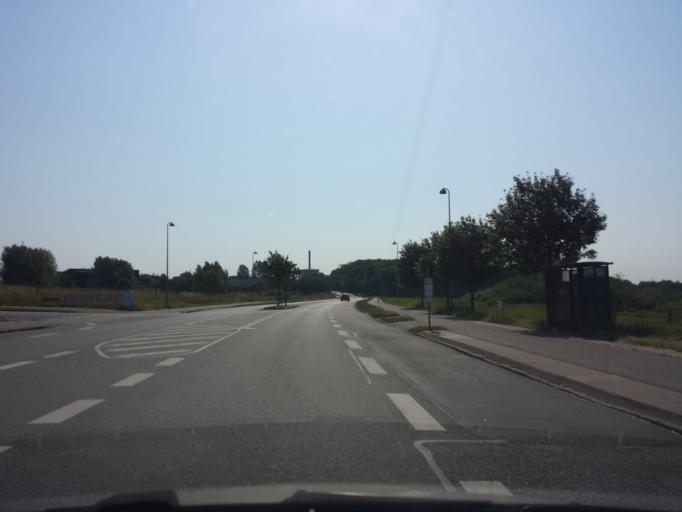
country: DK
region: Capital Region
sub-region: Ballerup Kommune
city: Malov
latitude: 55.7295
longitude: 12.3297
